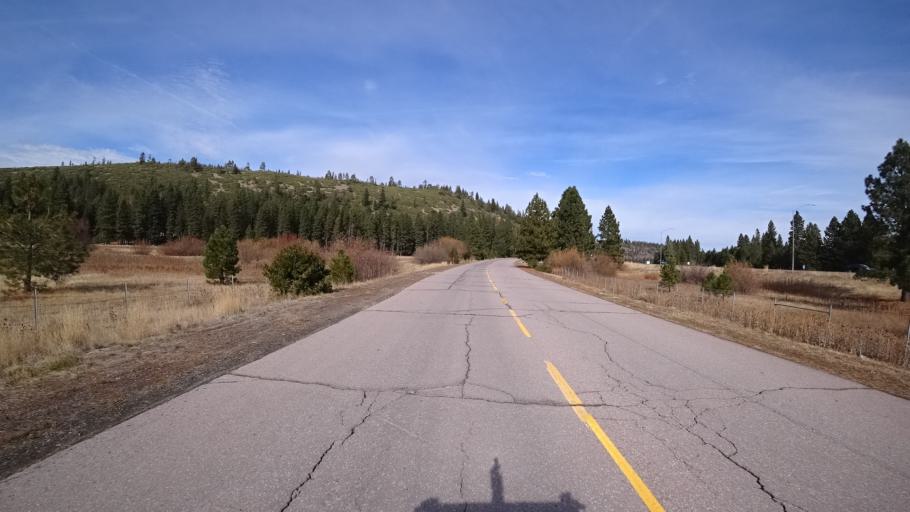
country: US
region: California
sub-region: Siskiyou County
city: Weed
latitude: 41.4006
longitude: -122.3840
